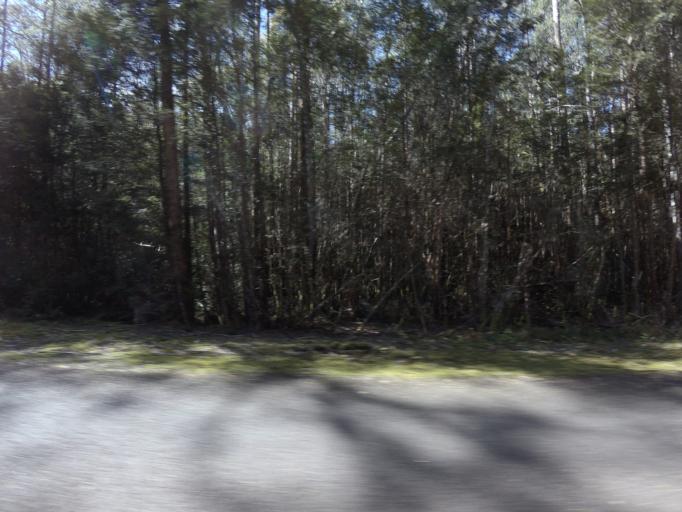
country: AU
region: Tasmania
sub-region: Derwent Valley
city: New Norfolk
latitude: -42.7327
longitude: 146.4259
